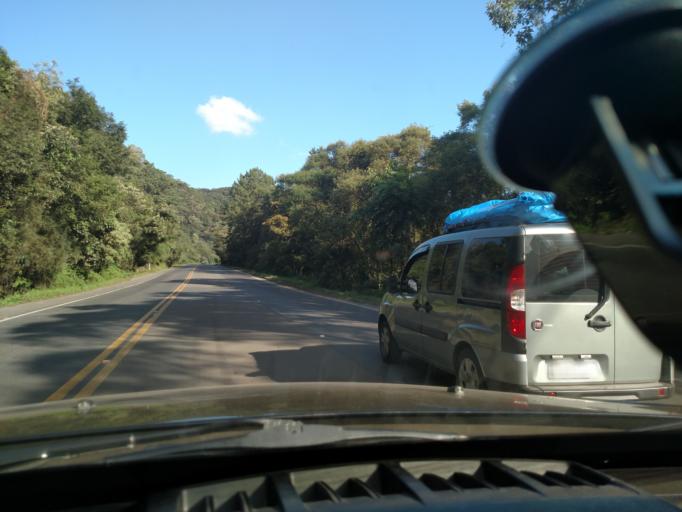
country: BR
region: Santa Catarina
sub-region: Otacilio Costa
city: Otacilio Costa
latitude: -27.2944
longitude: -50.0780
